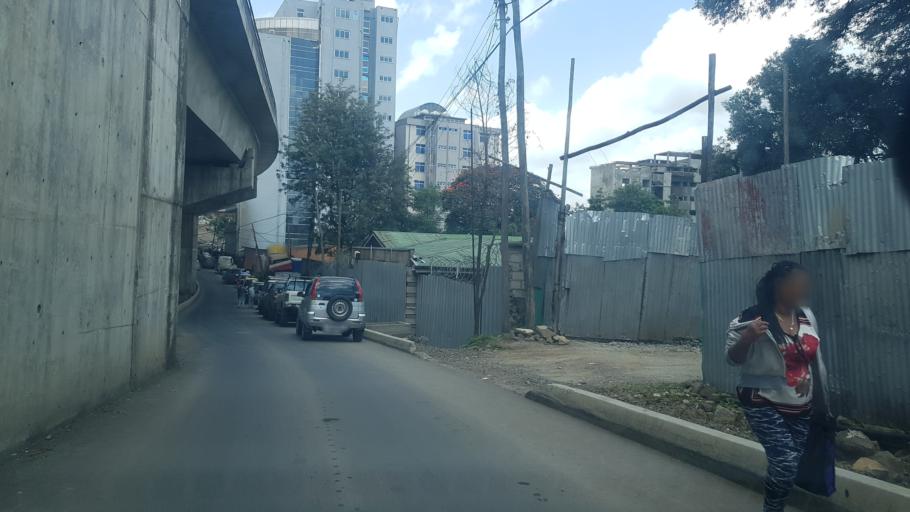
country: ET
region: Adis Abeba
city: Addis Ababa
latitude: 8.9957
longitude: 38.7581
